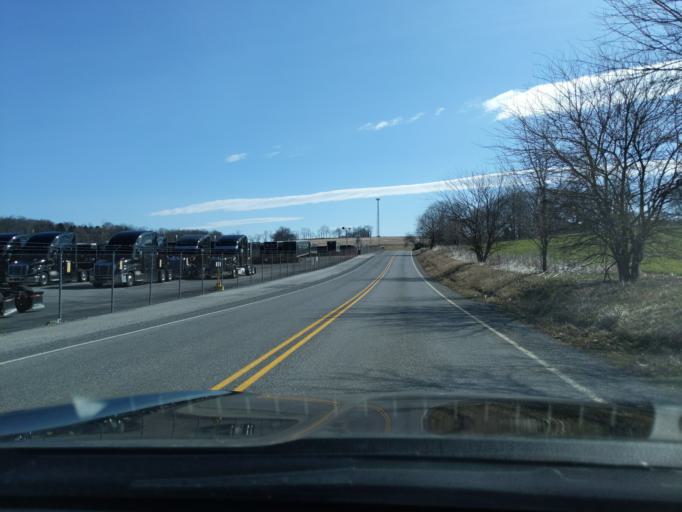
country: US
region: Pennsylvania
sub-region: Blair County
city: Roaring Spring
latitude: 40.3206
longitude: -78.3855
